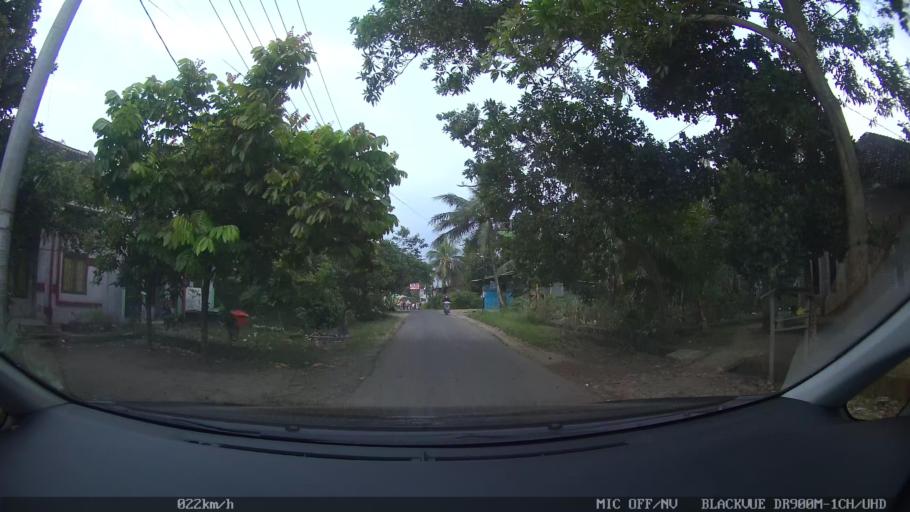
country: ID
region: Lampung
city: Kedaton
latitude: -5.3459
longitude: 105.2327
